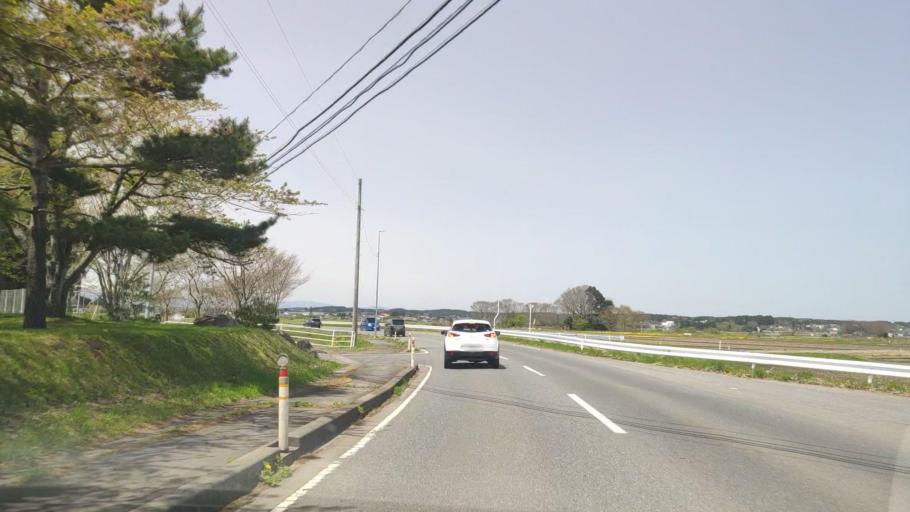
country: JP
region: Aomori
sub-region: Misawa Shi
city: Inuotose
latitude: 40.5936
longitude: 141.3417
